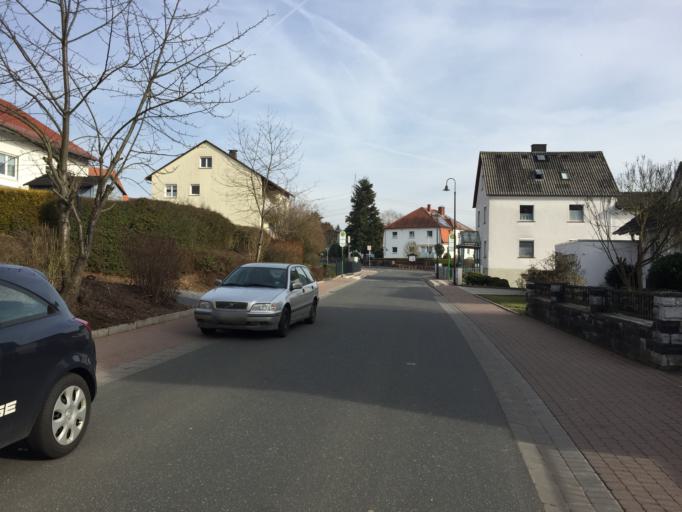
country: DE
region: Hesse
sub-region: Regierungsbezirk Giessen
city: Fronhausen
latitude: 50.6817
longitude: 8.6883
